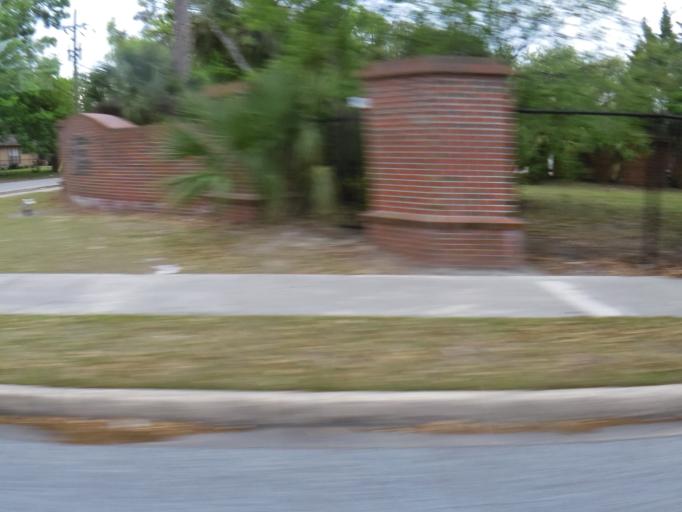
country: US
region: Florida
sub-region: Duval County
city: Jacksonville
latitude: 30.2990
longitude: -81.6316
